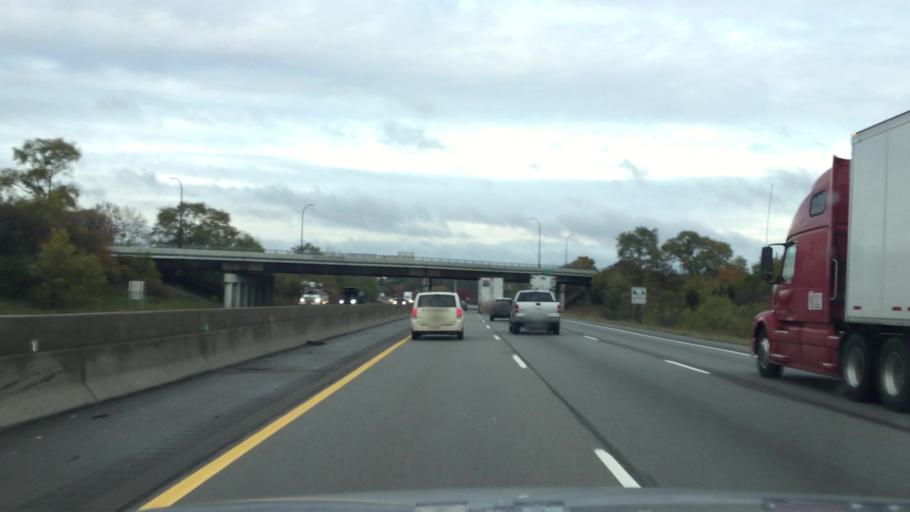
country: US
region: Michigan
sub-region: Washtenaw County
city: Ypsilanti
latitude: 42.2316
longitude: -83.5982
